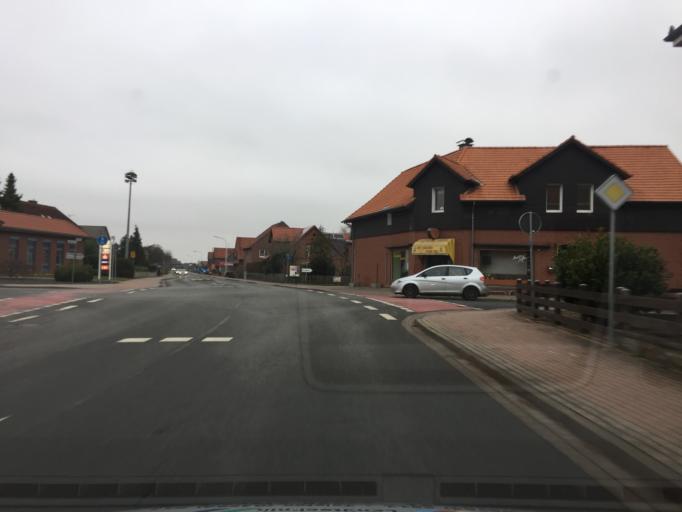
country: DE
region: Lower Saxony
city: Meerbeck
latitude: 52.3422
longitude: 9.1449
